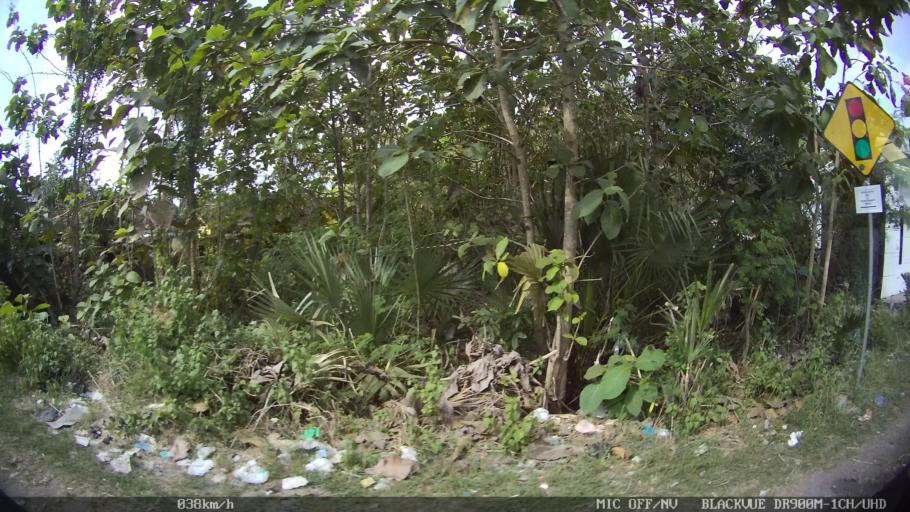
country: ID
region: Daerah Istimewa Yogyakarta
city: Kasihan
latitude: -7.8384
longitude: 110.3125
